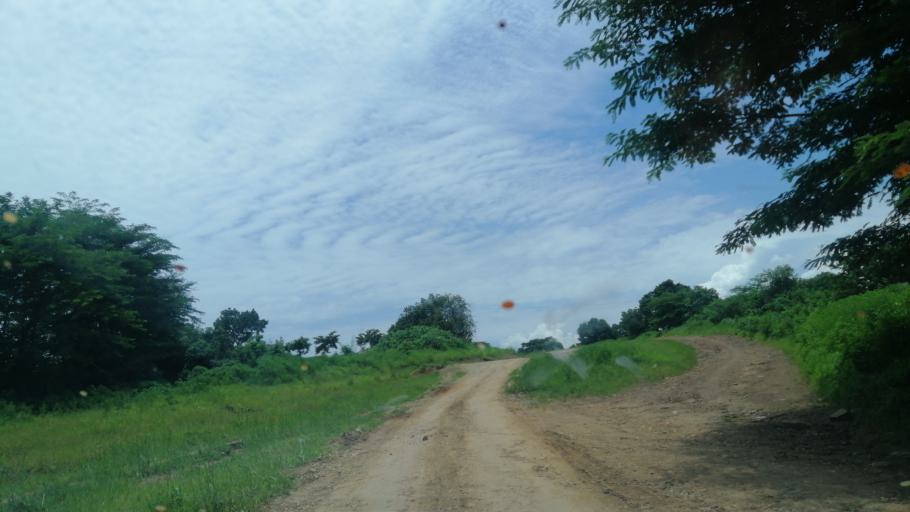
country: ET
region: Oromiya
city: Mendi
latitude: 10.1688
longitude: 35.0916
